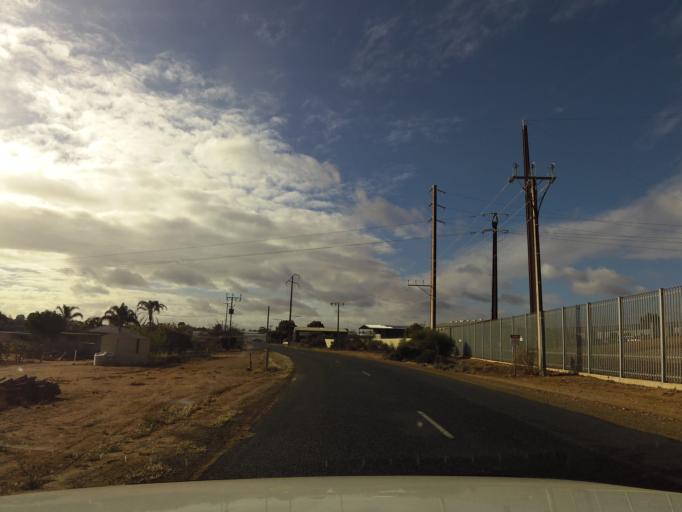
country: AU
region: South Australia
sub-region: Berri and Barmera
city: Berri
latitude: -34.2694
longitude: 140.5981
